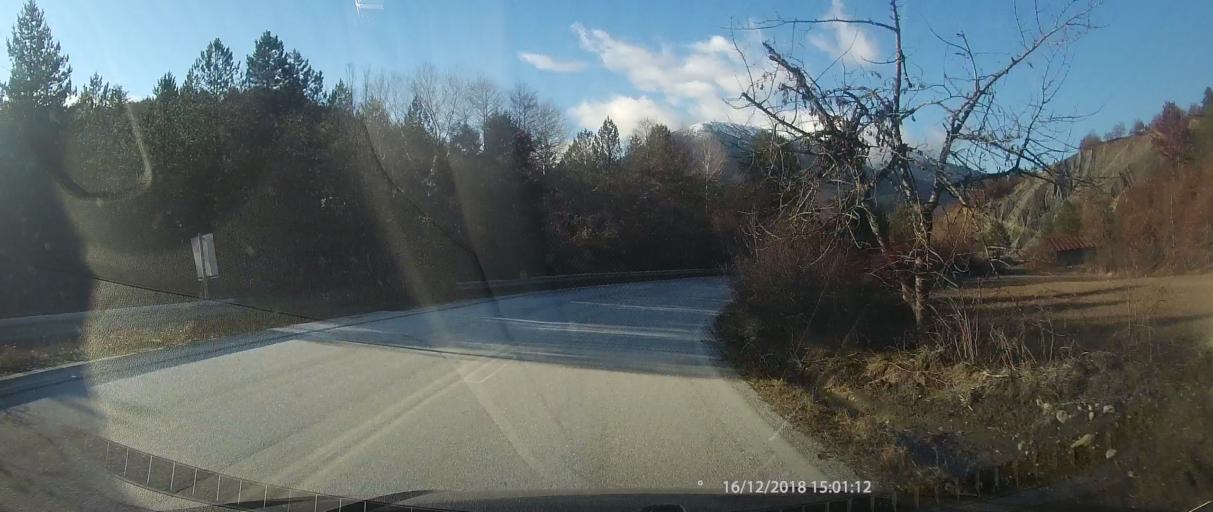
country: GR
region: West Macedonia
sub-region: Nomos Kastorias
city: Nestorio
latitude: 40.2194
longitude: 21.0084
